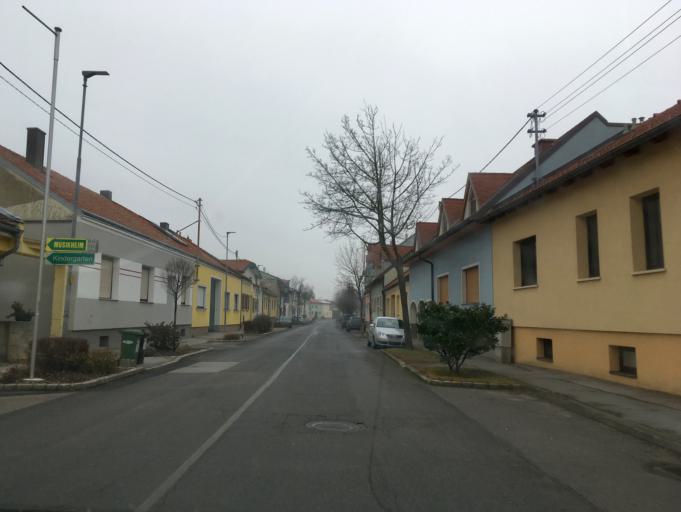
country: AT
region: Lower Austria
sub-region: Politischer Bezirk Bruck an der Leitha
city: Trautmannsdorf an der Leitha
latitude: 48.0535
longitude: 16.6437
